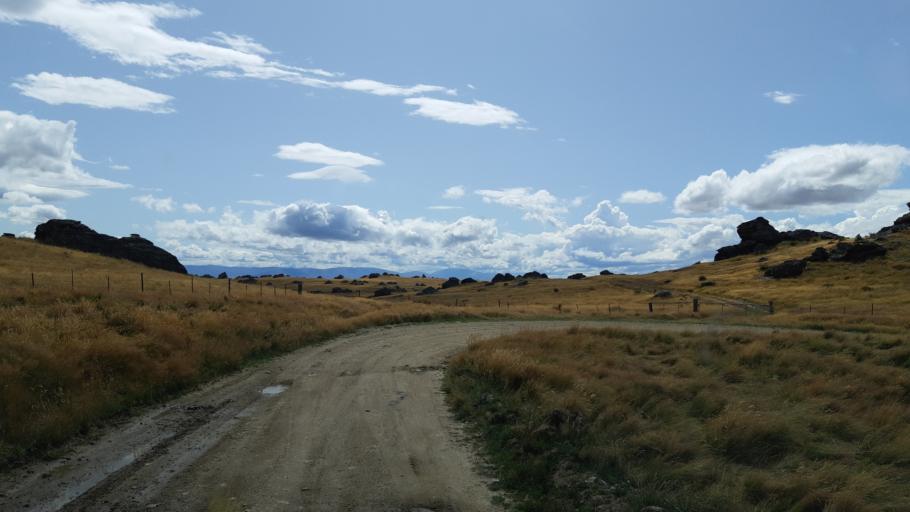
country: NZ
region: Otago
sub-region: Queenstown-Lakes District
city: Wanaka
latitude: -45.2942
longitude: 169.7386
